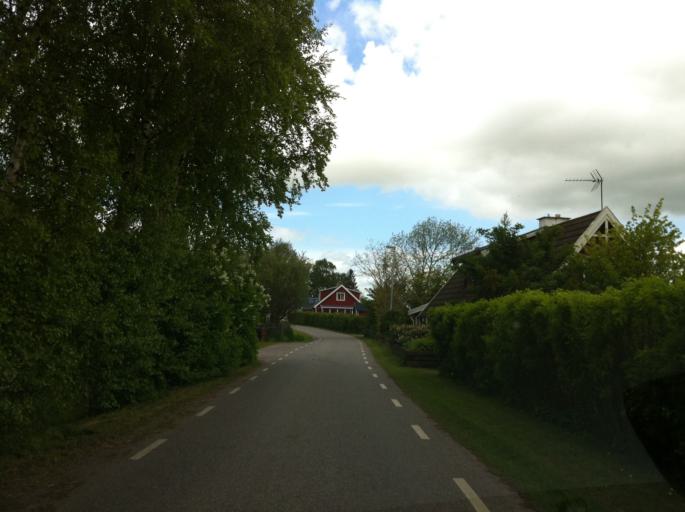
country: SE
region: Skane
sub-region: Svalovs Kommun
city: Teckomatorp
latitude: 55.8542
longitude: 13.0632
